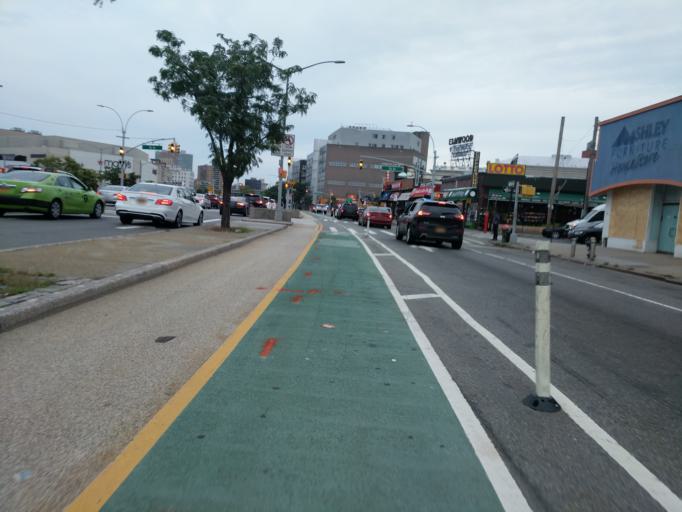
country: US
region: New York
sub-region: Queens County
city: Borough of Queens
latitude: 40.7349
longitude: -73.8752
